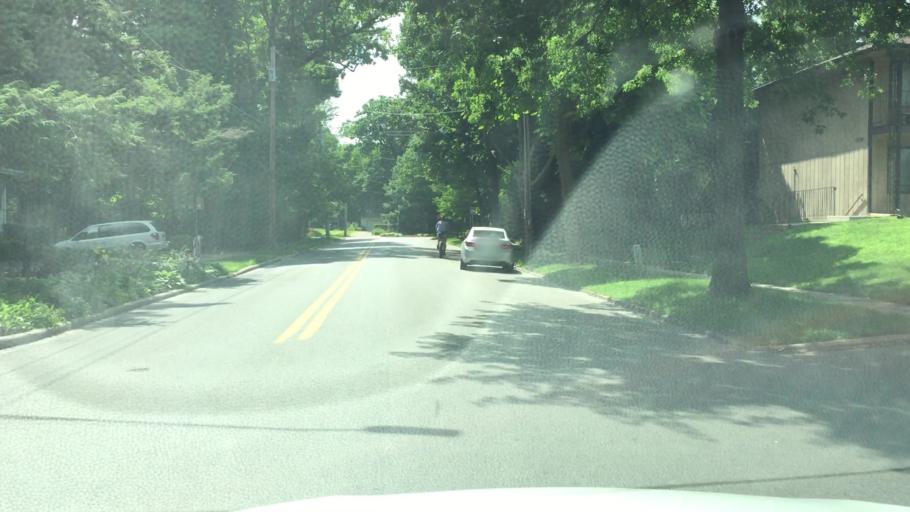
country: US
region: Iowa
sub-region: Johnson County
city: Iowa City
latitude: 41.6567
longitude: -91.5198
